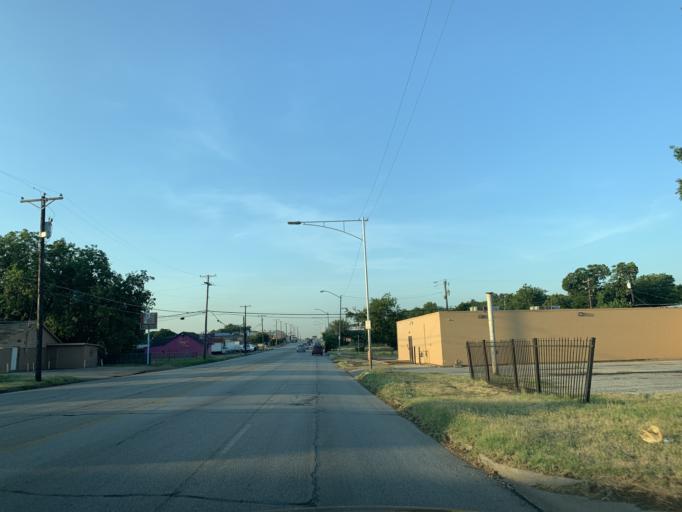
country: US
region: Texas
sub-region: Tarrant County
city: Blue Mound
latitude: 32.8104
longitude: -97.3516
